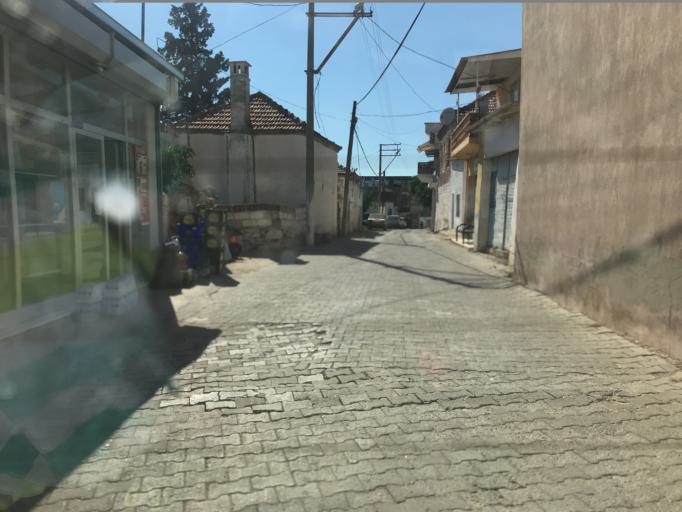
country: TR
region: Mugla
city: Selimiye
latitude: 37.3717
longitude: 27.4923
